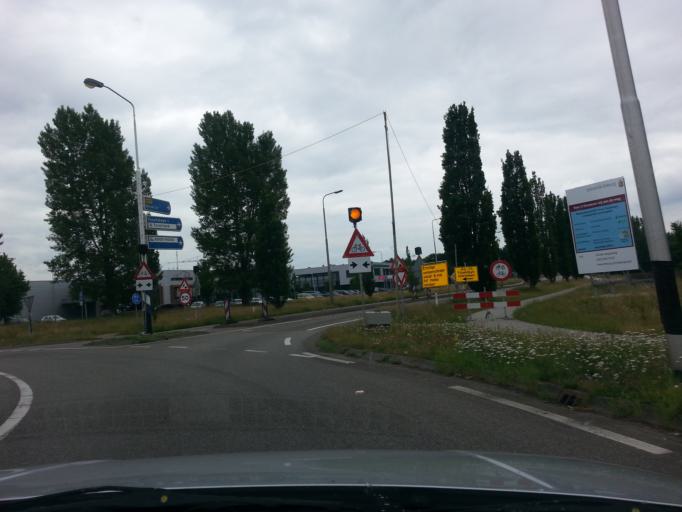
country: NL
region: Limburg
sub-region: Gemeente Venray
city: Venray
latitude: 51.4971
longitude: 5.8922
